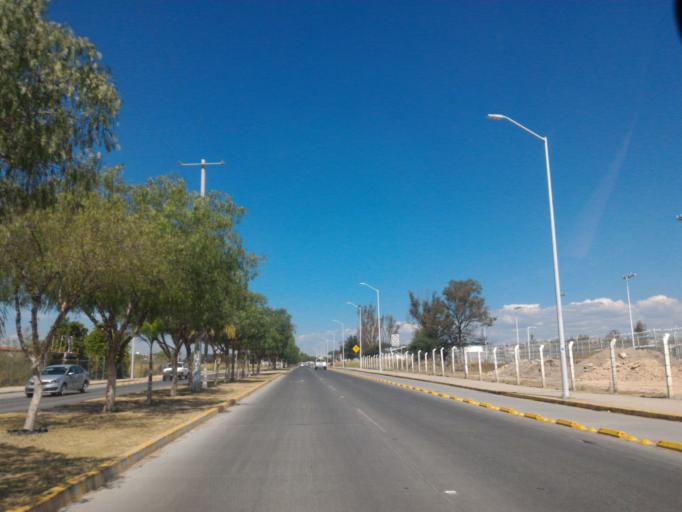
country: MX
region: Guanajuato
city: San Francisco del Rincon
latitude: 21.0327
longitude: -101.8695
